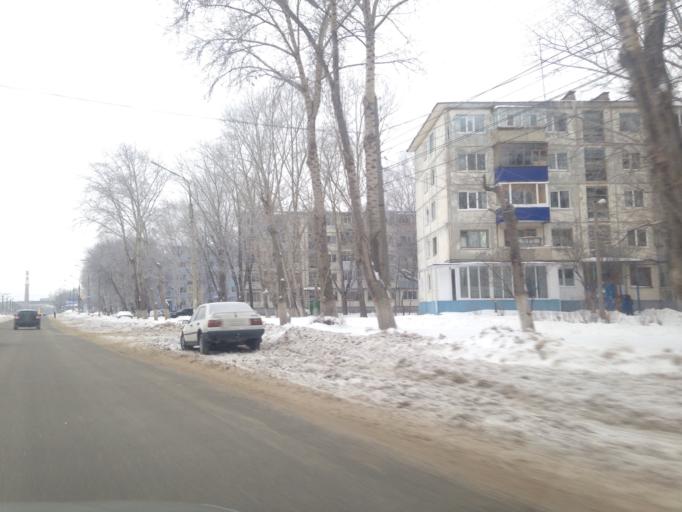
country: RU
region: Ulyanovsk
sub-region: Ulyanovskiy Rayon
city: Ulyanovsk
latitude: 54.3013
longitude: 48.3456
